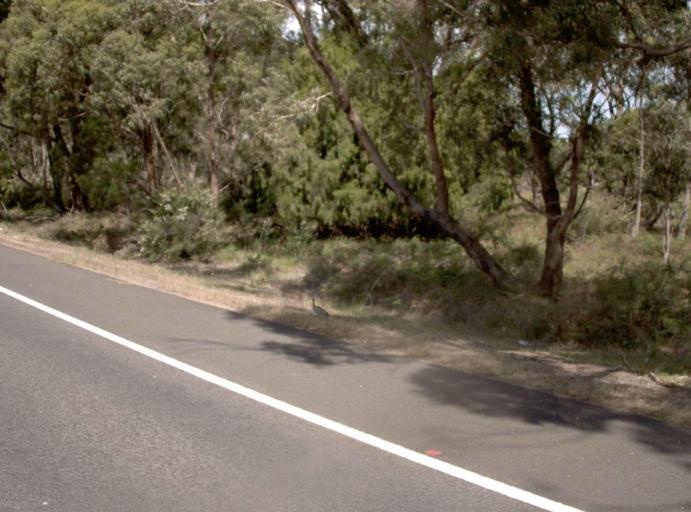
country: AU
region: Victoria
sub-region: East Gippsland
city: Bairnsdale
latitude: -37.9067
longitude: 147.3286
